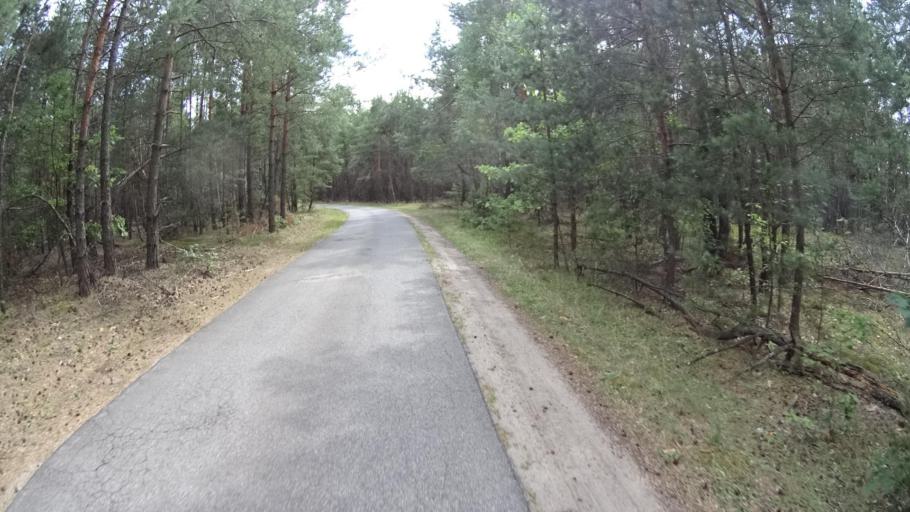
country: PL
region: Masovian Voivodeship
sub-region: Powiat bialobrzeski
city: Bialobrzegi
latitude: 51.6383
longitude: 20.9022
